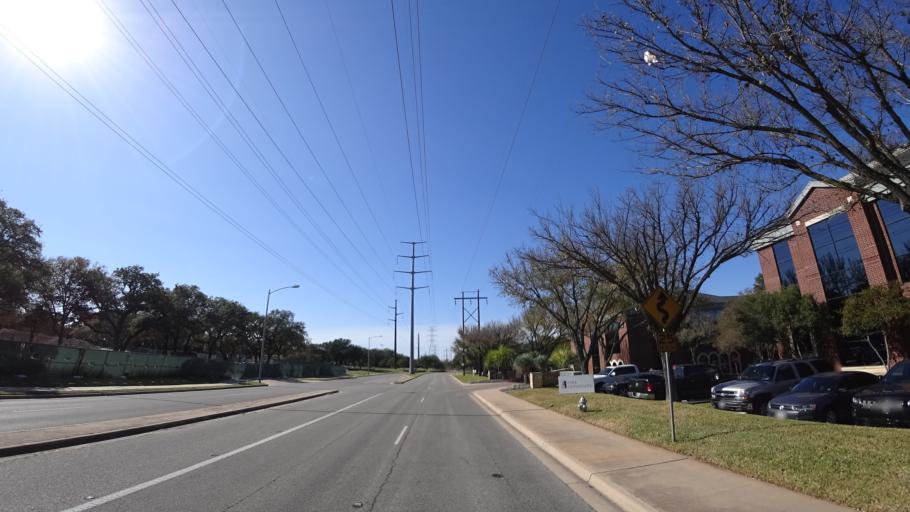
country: US
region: Texas
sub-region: Williamson County
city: Jollyville
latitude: 30.4007
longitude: -97.7497
